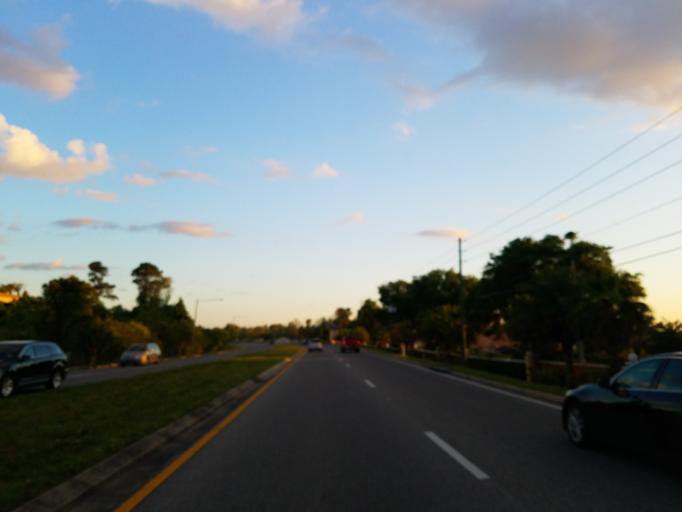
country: US
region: Florida
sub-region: Orange County
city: Doctor Phillips
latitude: 28.4227
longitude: -81.4757
